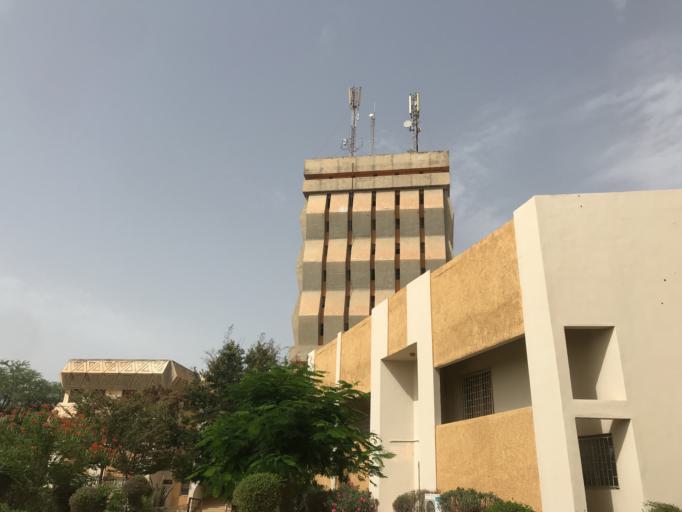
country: SN
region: Saint-Louis
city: Saint-Louis
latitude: 16.0613
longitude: -16.4234
